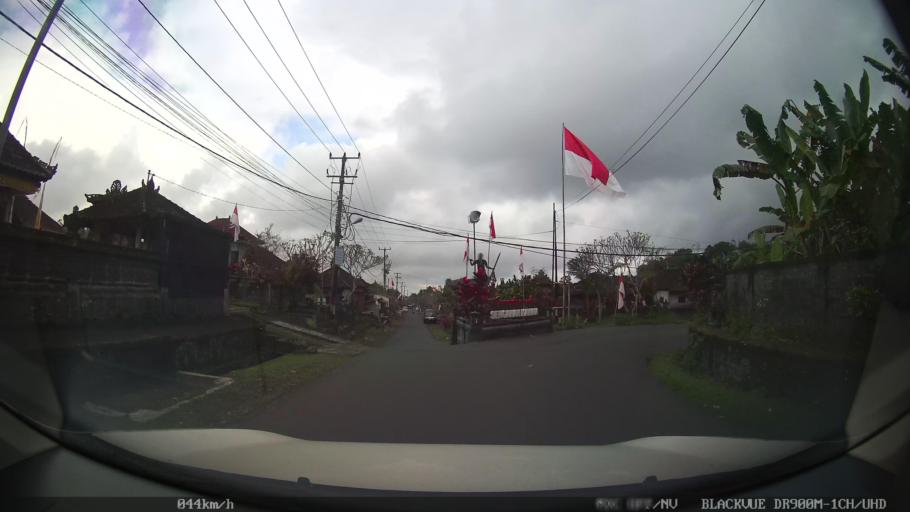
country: ID
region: Bali
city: Empalan
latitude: -8.3744
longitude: 115.1568
